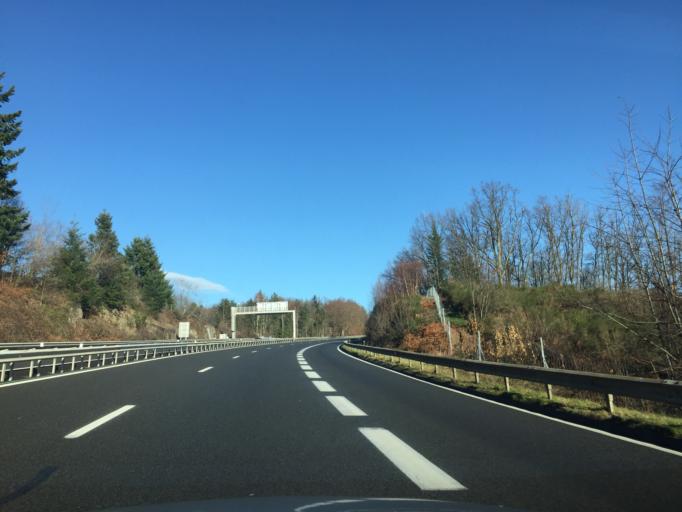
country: FR
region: Auvergne
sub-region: Departement du Puy-de-Dome
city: Thiers
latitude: 45.8719
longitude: 3.5617
